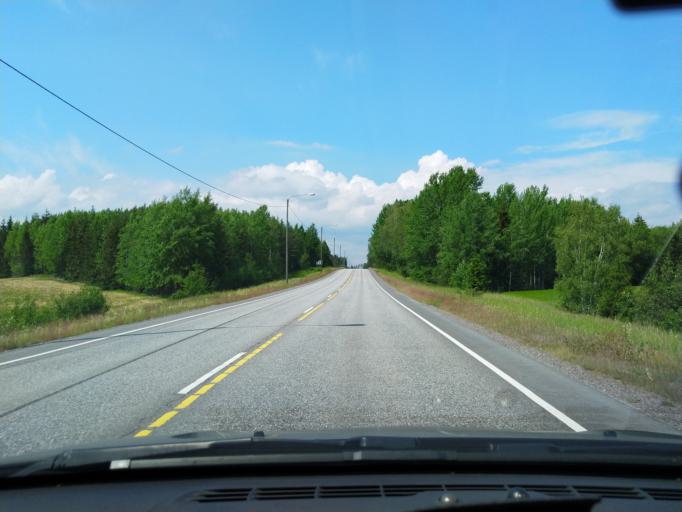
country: FI
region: Uusimaa
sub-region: Helsinki
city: Saukkola
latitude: 60.3763
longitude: 24.1019
